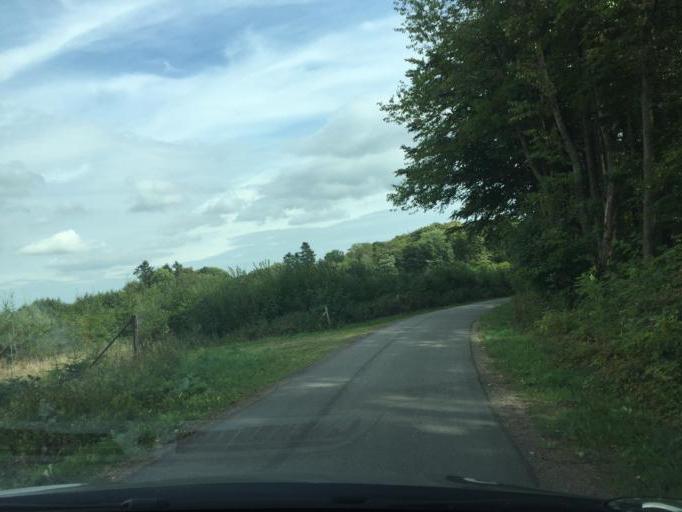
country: DK
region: South Denmark
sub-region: Assens Kommune
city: Vissenbjerg
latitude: 55.4150
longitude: 10.2074
